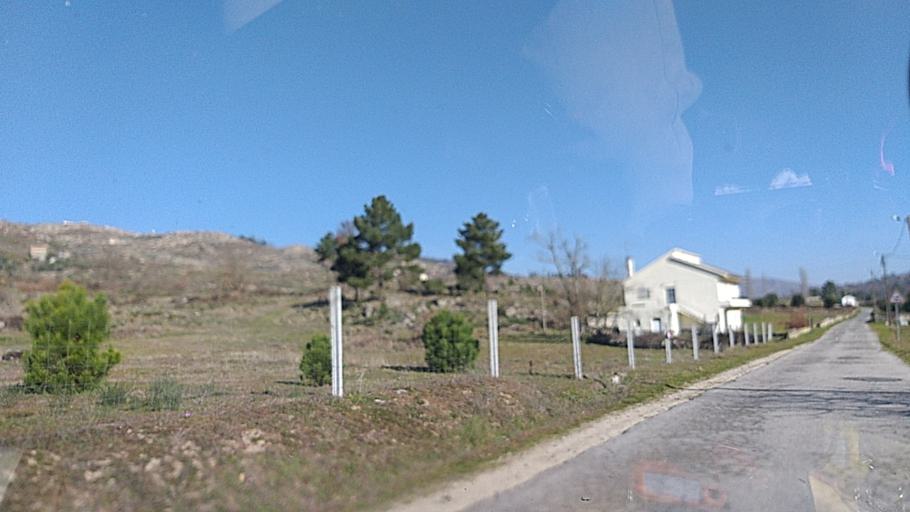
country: PT
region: Guarda
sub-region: Celorico da Beira
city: Celorico da Beira
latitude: 40.6634
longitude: -7.4606
